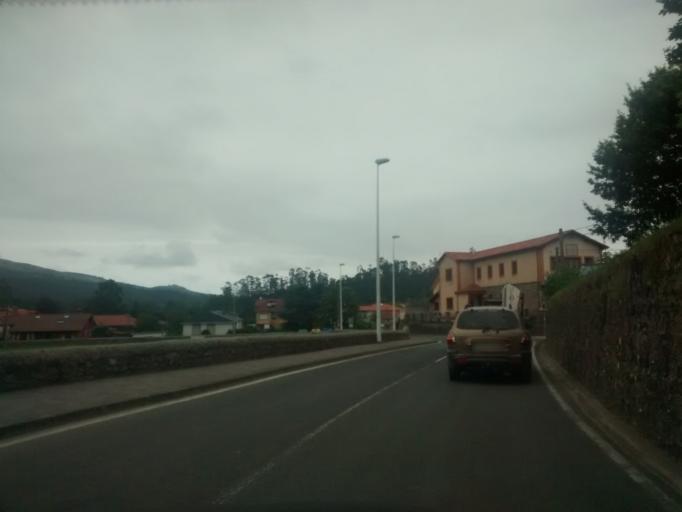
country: ES
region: Cantabria
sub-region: Provincia de Cantabria
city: Luzmela
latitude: 43.3156
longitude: -4.1927
